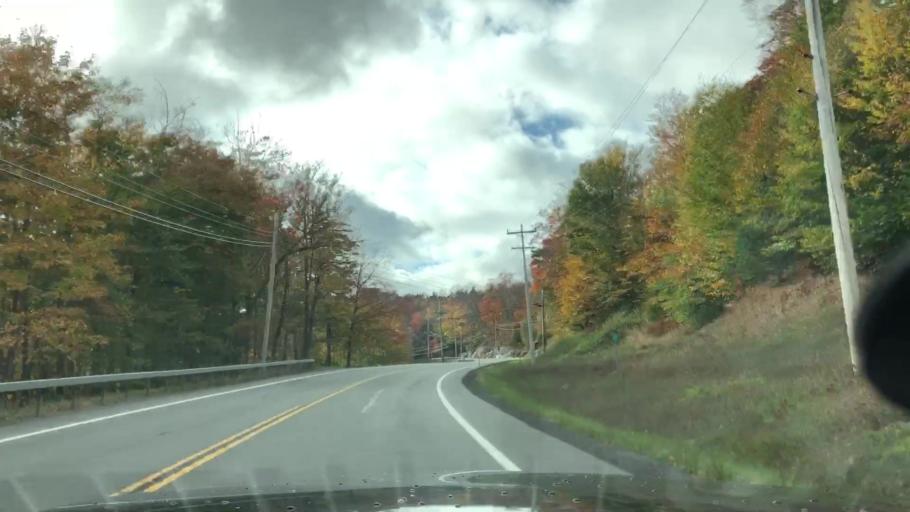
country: US
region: New York
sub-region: Oneida County
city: Boonville
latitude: 43.7329
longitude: -74.9157
